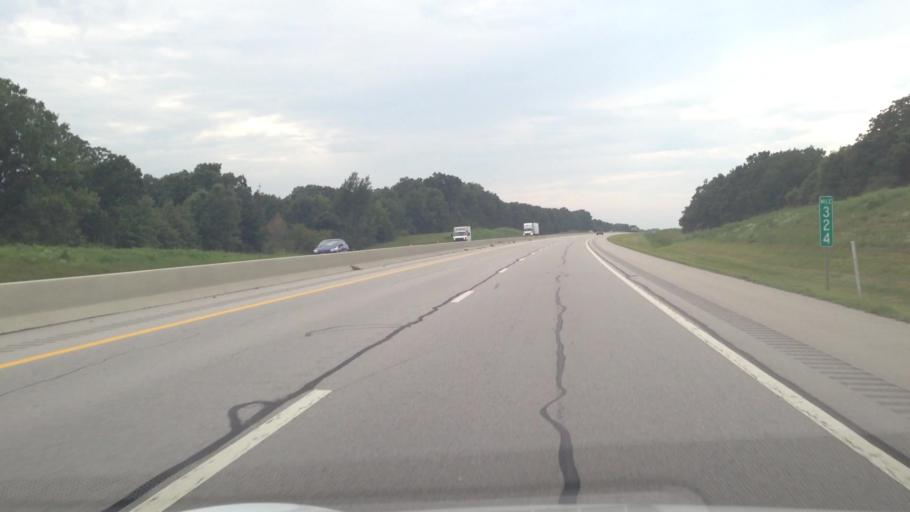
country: US
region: Kansas
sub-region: Cherokee County
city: Baxter Springs
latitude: 36.9408
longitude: -94.6908
